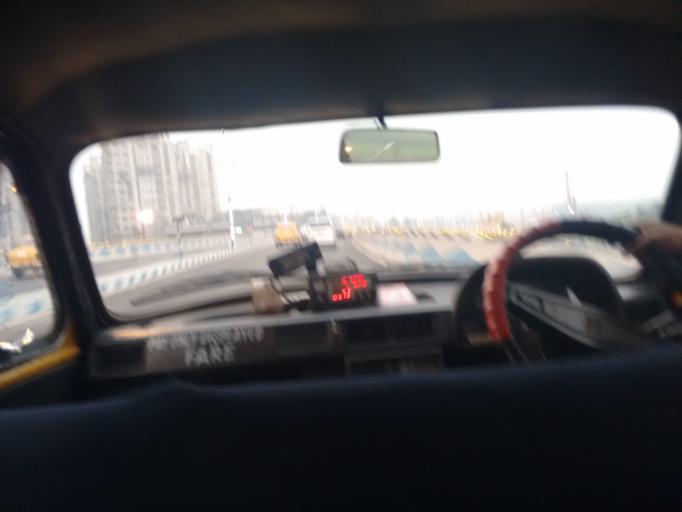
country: IN
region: West Bengal
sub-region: Kolkata
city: Kolkata
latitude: 22.5474
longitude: 88.3999
